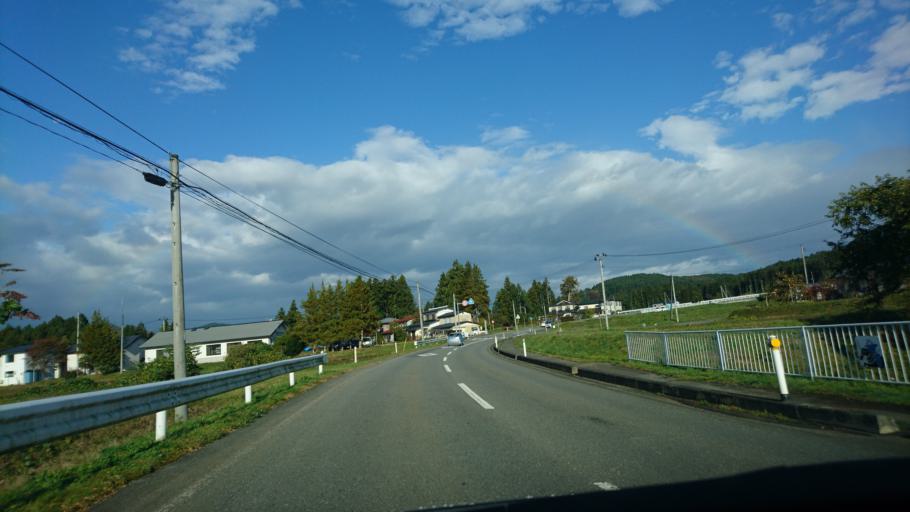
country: JP
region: Iwate
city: Mizusawa
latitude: 39.0400
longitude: 141.0620
